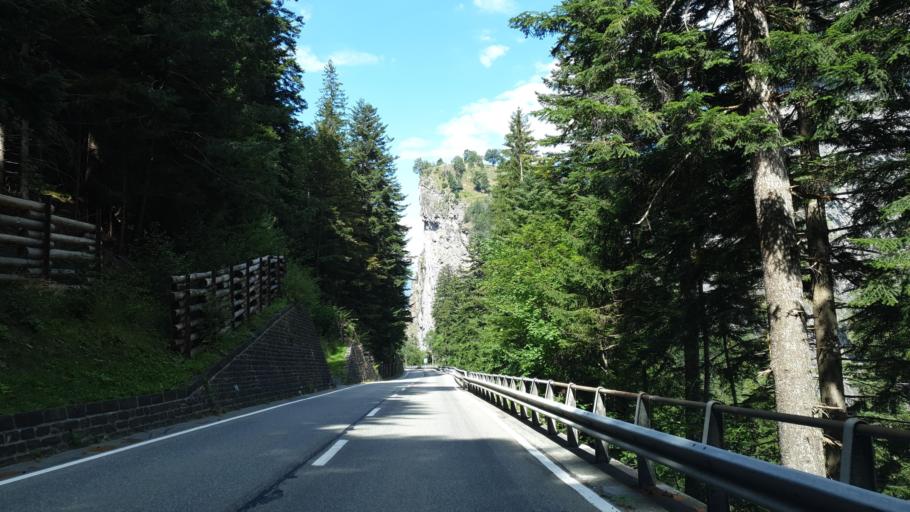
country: CH
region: Grisons
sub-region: Hinterrhein District
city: Thusis
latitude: 46.6849
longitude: 9.4456
